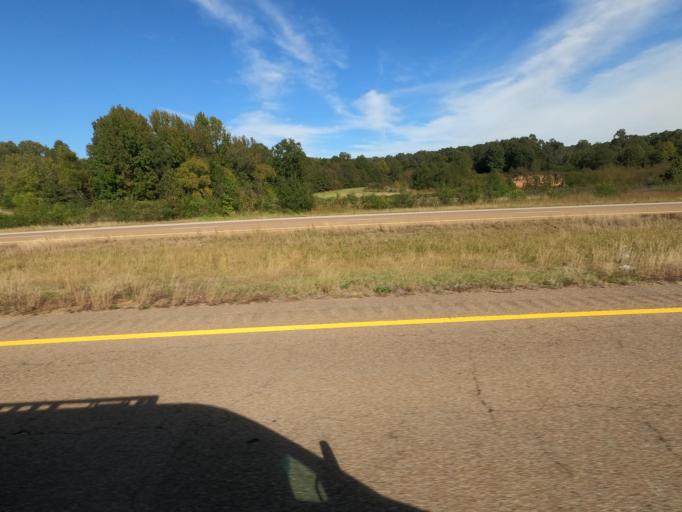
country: US
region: Tennessee
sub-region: Fayette County
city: Hickory Withe
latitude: 35.1764
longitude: -89.6479
